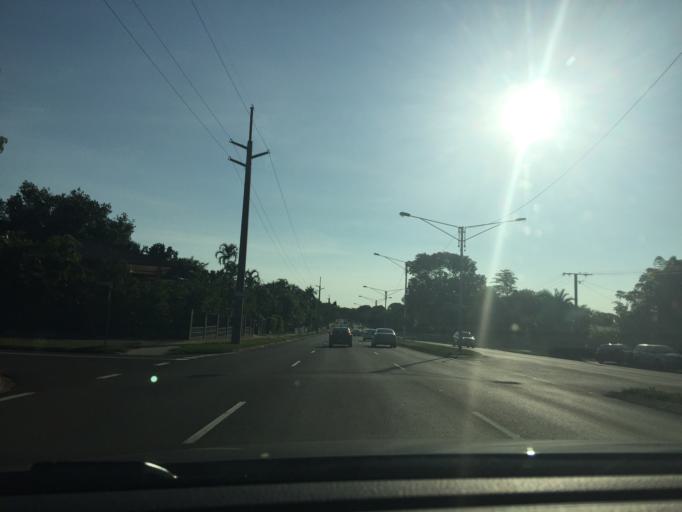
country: AU
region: Northern Territory
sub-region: Darwin
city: Nightcliff
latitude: -12.3839
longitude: 130.8703
